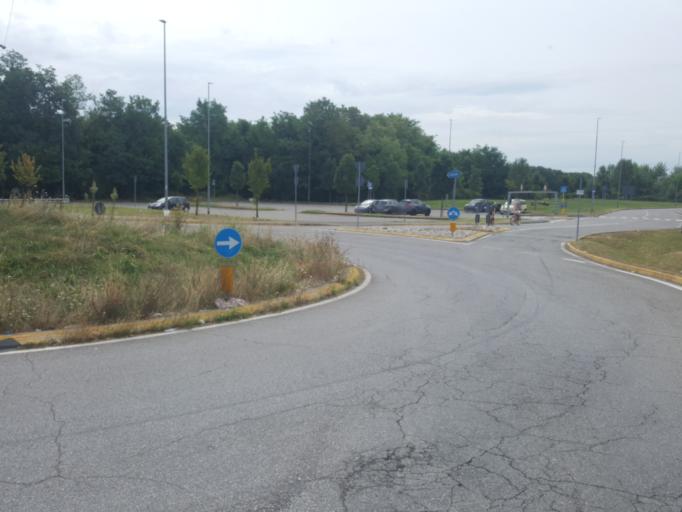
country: IT
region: Lombardy
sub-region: Citta metropolitana di Milano
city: Basiano
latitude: 45.5803
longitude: 9.4593
